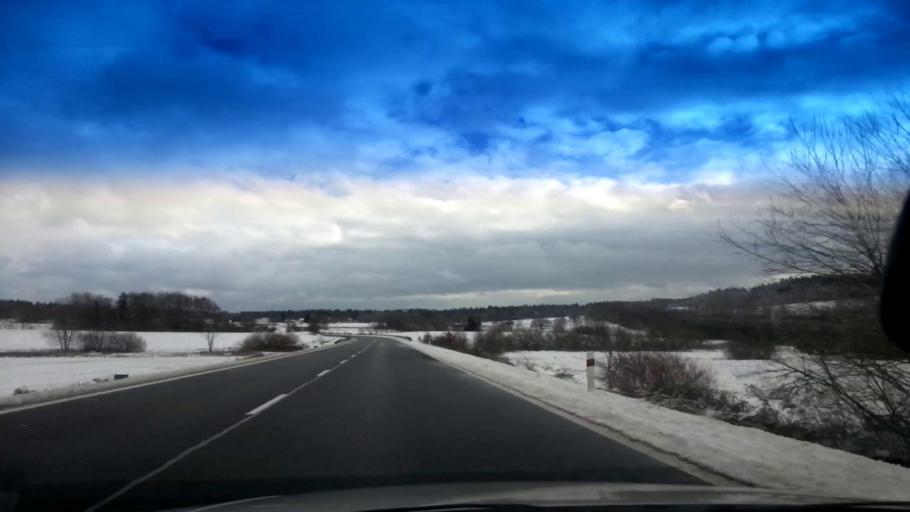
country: CZ
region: Karlovarsky
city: As
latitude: 50.2005
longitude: 12.1995
